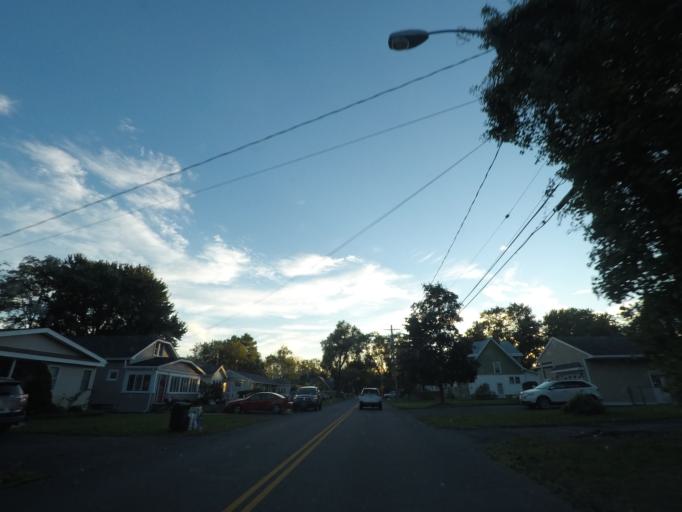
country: US
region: New York
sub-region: Albany County
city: Colonie
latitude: 42.7178
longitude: -73.8301
